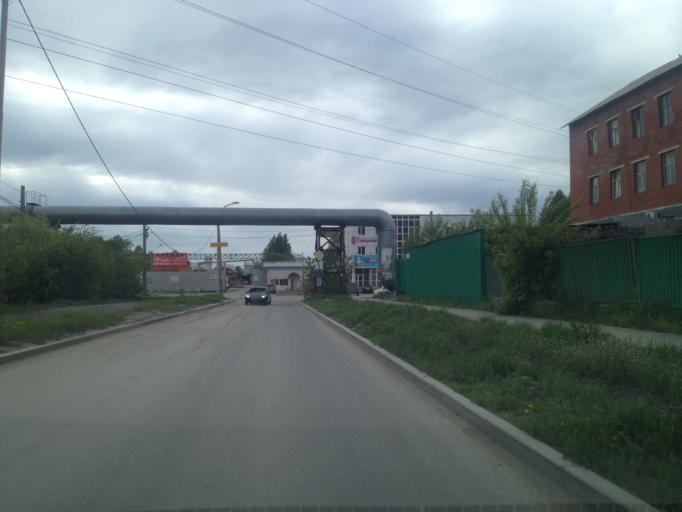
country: RU
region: Sverdlovsk
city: Yekaterinburg
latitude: 56.8738
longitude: 60.5428
